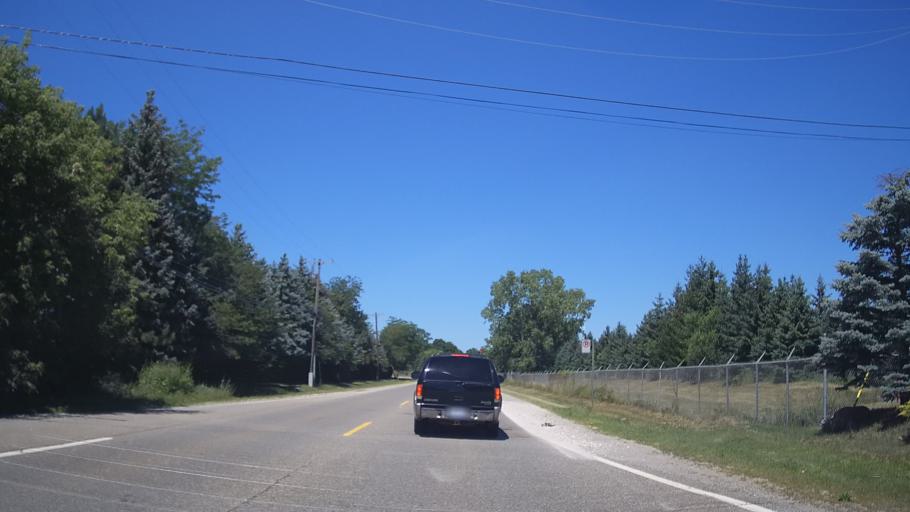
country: US
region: Michigan
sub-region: Macomb County
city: Shelby
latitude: 42.6530
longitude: -83.0856
